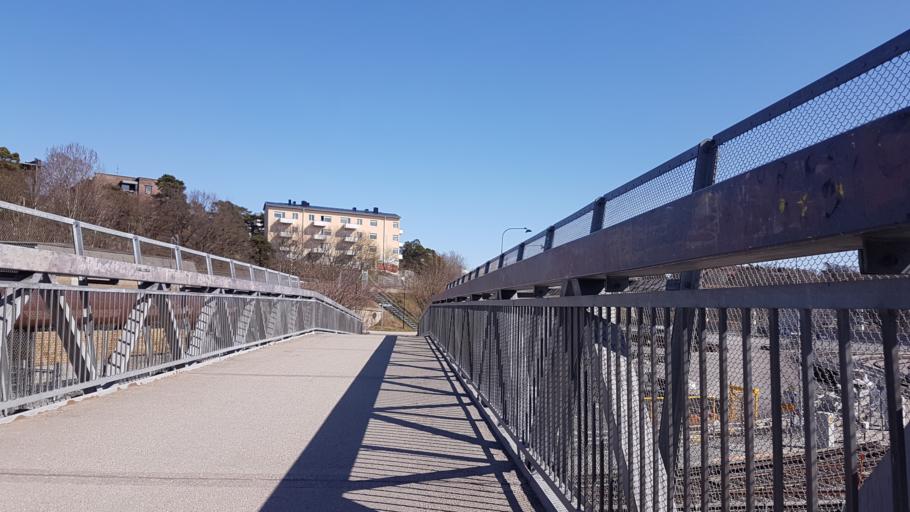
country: SE
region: Stockholm
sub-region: Stockholms Kommun
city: Arsta
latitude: 59.2941
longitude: 18.0918
